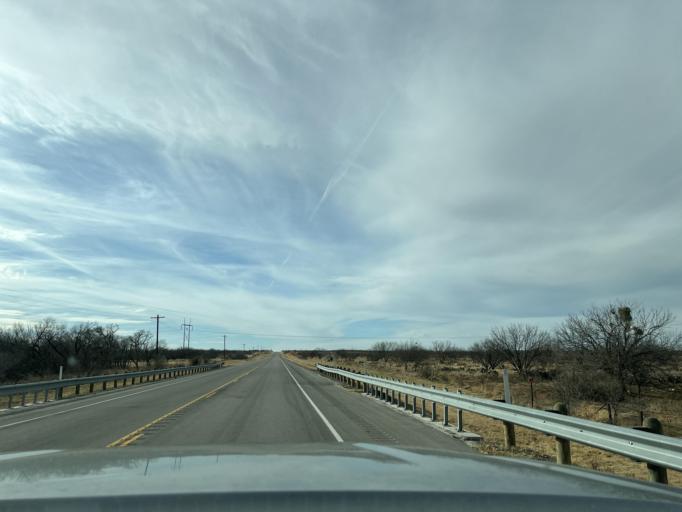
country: US
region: Texas
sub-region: Jones County
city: Anson
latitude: 32.7508
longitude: -99.7292
